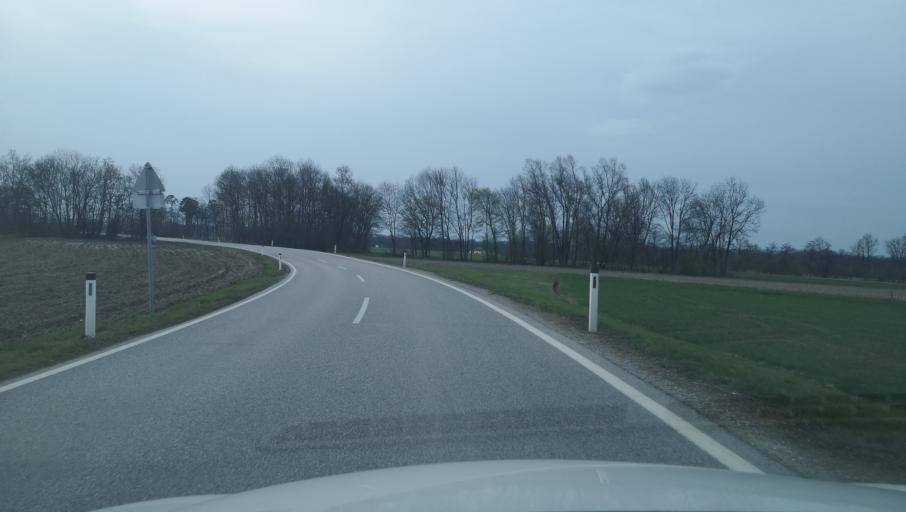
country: AT
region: Lower Austria
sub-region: Politischer Bezirk Amstetten
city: Euratsfeld
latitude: 48.0966
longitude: 14.9227
